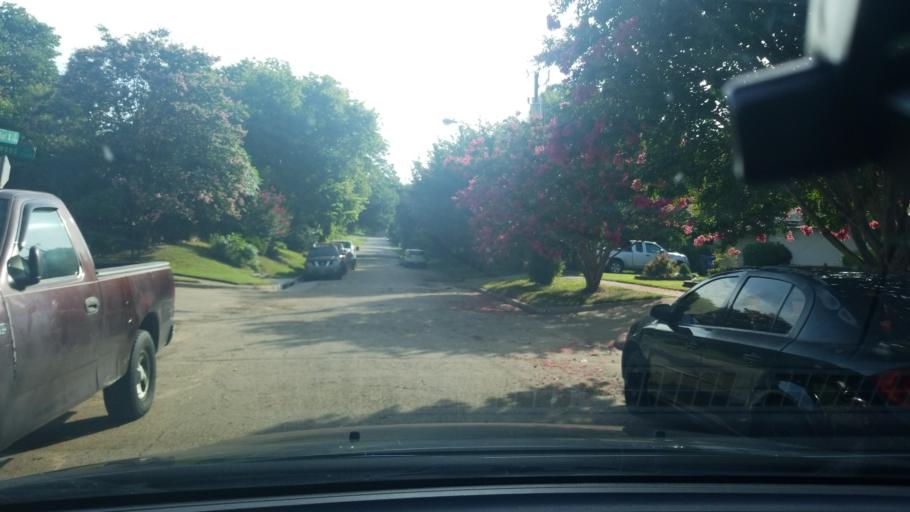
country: US
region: Texas
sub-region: Dallas County
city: Highland Park
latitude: 32.7982
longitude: -96.7133
